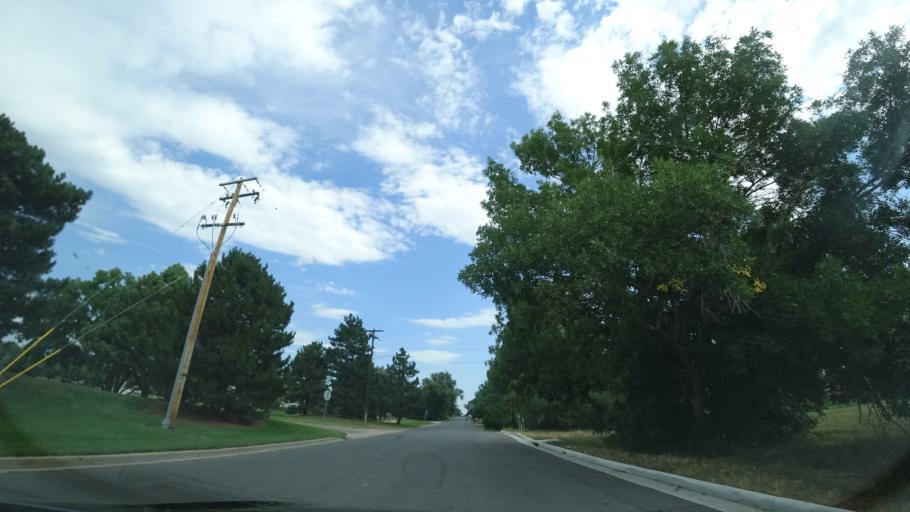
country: US
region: Colorado
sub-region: Jefferson County
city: Lakewood
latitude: 39.7191
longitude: -105.0698
